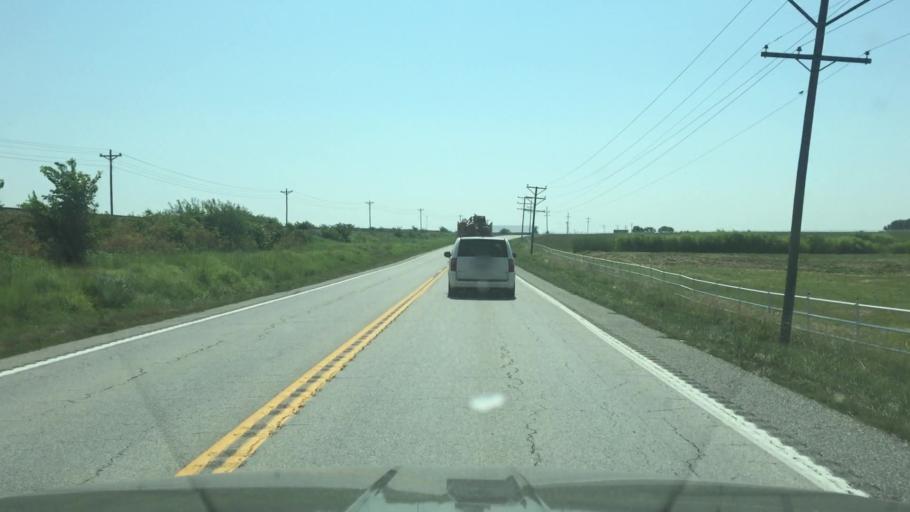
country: US
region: Missouri
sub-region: Moniteau County
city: Tipton
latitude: 38.6705
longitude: -92.8487
